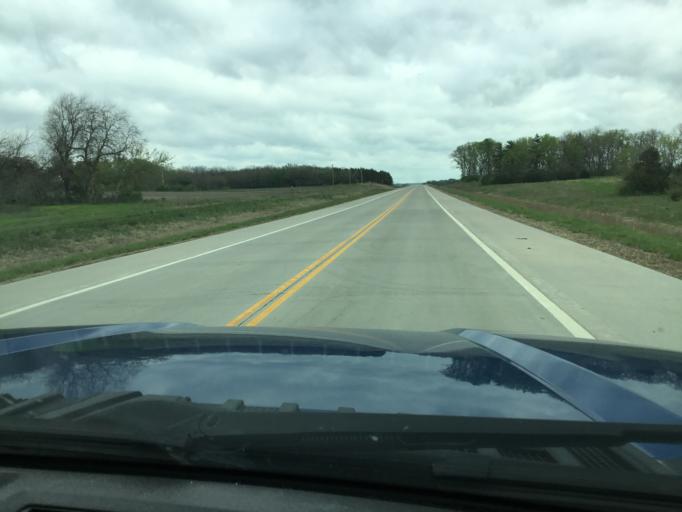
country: US
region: Kansas
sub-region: Douglas County
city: Lawrence
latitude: 38.9343
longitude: -95.1768
